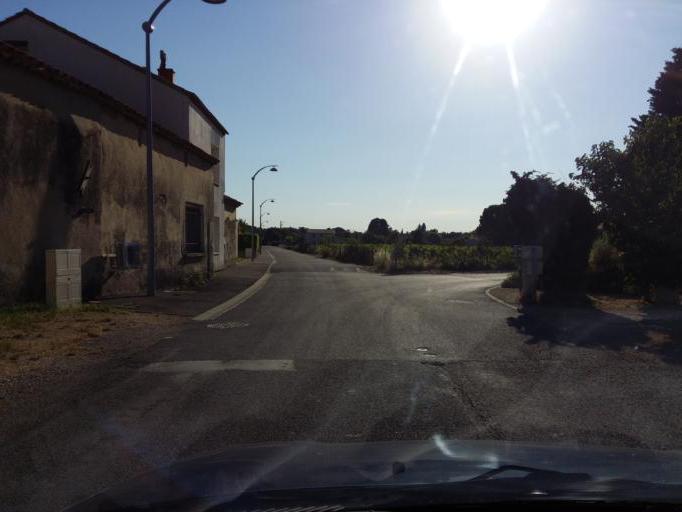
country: FR
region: Provence-Alpes-Cote d'Azur
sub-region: Departement du Vaucluse
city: Camaret-sur-Aigues
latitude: 44.1672
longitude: 4.8827
